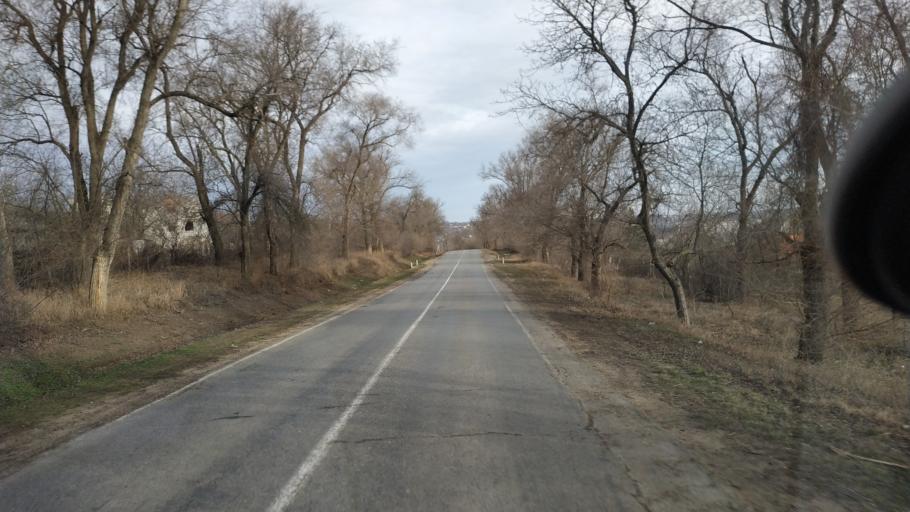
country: MD
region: Chisinau
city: Vadul lui Voda
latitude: 47.1231
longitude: 29.0638
